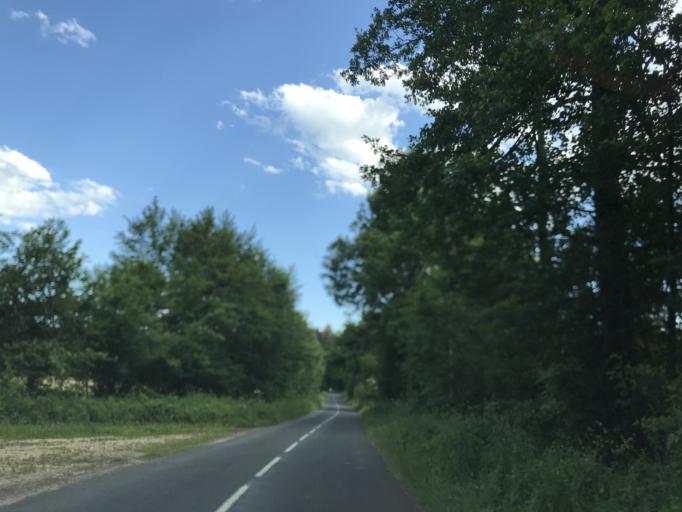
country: FR
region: Auvergne
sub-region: Departement du Puy-de-Dome
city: Courpiere
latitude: 45.7698
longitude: 3.6004
